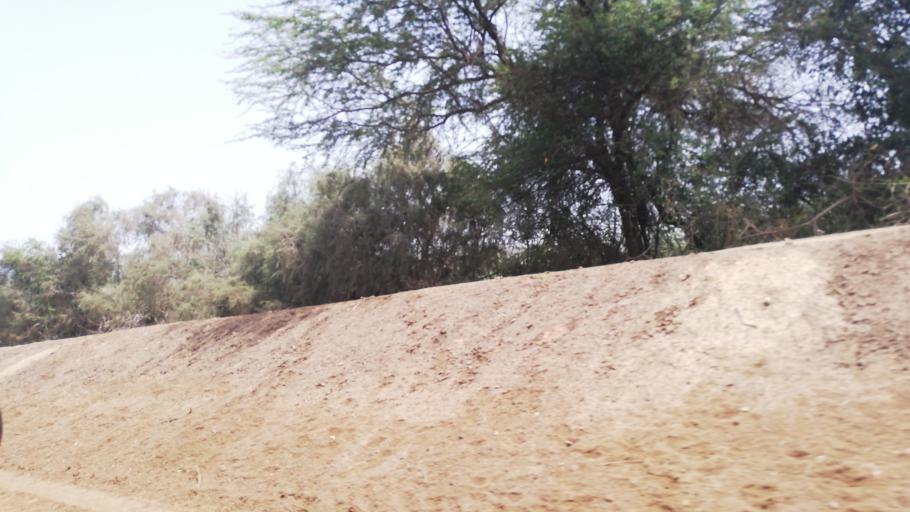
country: SN
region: Saint-Louis
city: Saint-Louis
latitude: 16.4051
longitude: -16.2957
